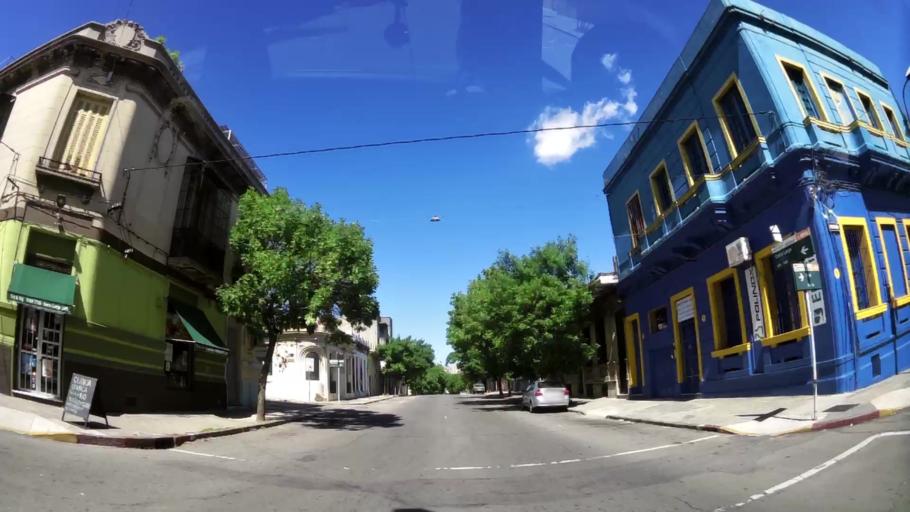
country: UY
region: Montevideo
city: Montevideo
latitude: -34.8994
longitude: -56.1830
